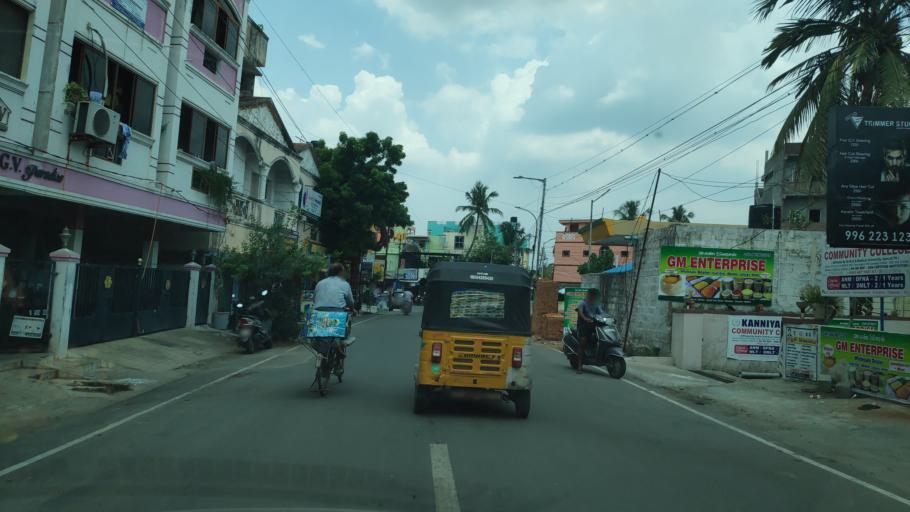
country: IN
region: Tamil Nadu
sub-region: Thiruvallur
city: Ambattur
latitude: 13.1176
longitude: 80.1562
